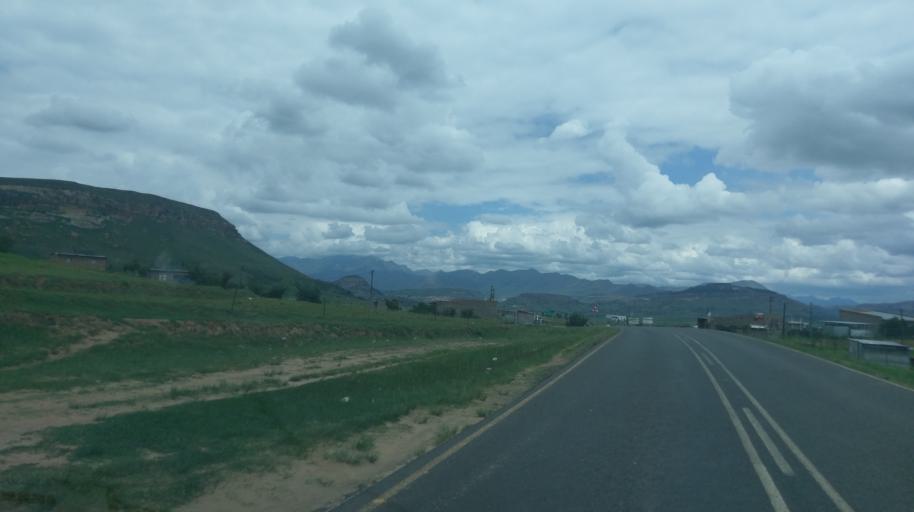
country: LS
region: Leribe
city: Leribe
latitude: -28.9483
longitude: 28.1691
